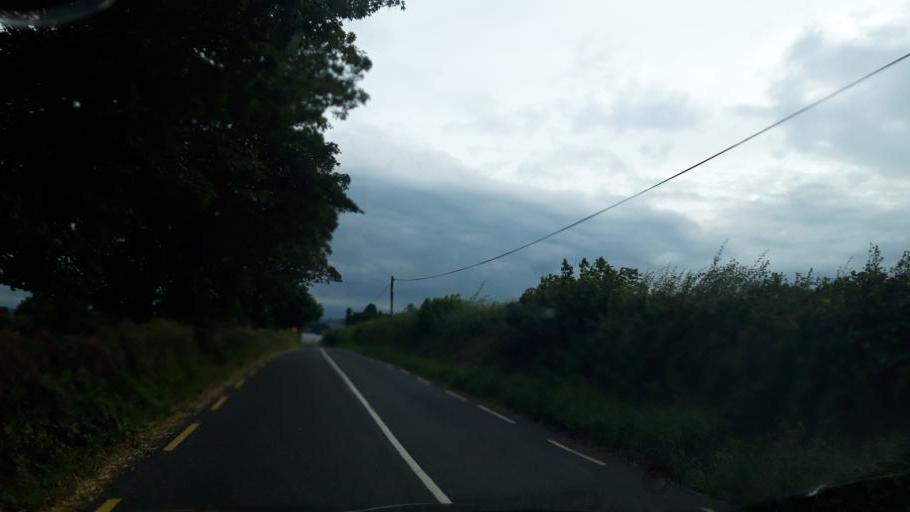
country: IE
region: Leinster
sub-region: Kilkenny
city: Ballyragget
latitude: 52.7562
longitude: -7.3908
